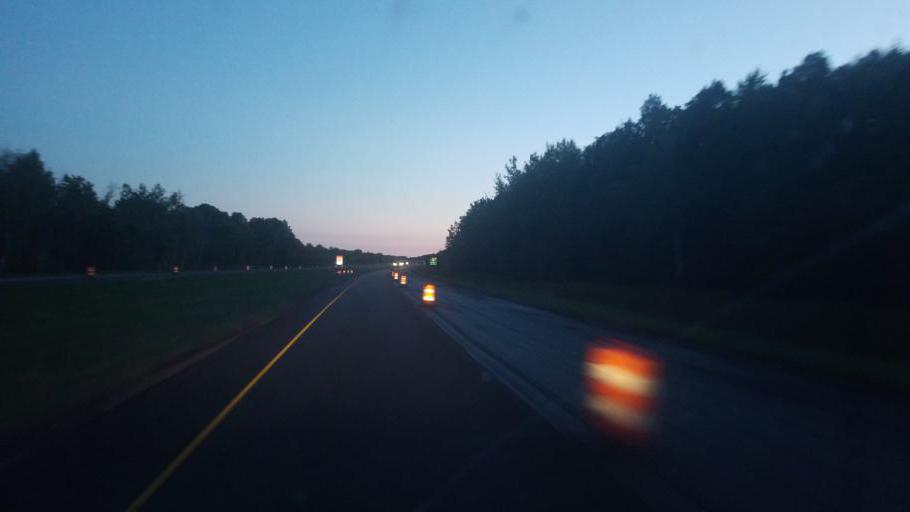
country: US
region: Ohio
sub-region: Ashtabula County
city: Jefferson
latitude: 41.7169
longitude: -80.7076
